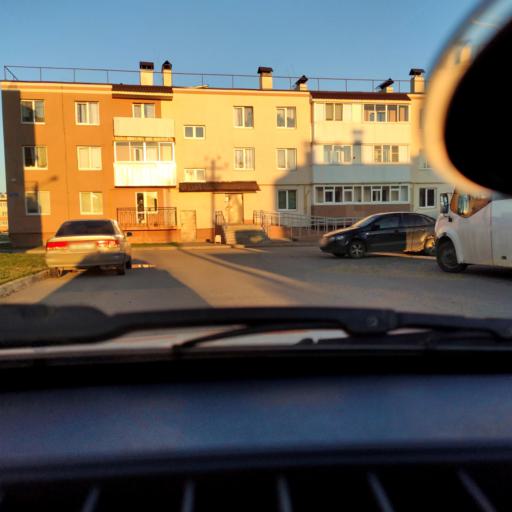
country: RU
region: Bashkortostan
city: Ufa
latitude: 54.8334
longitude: 56.1678
